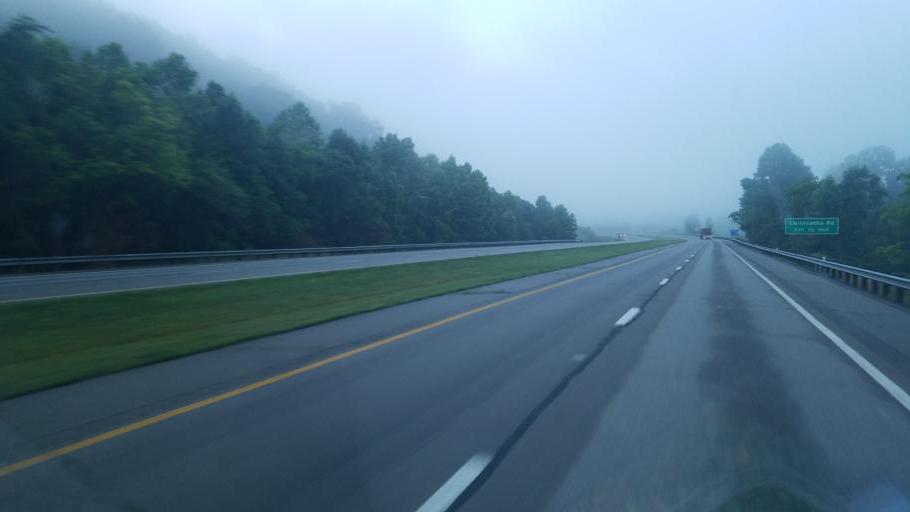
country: US
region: Ohio
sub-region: Jackson County
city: Jackson
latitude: 39.1015
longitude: -82.6702
